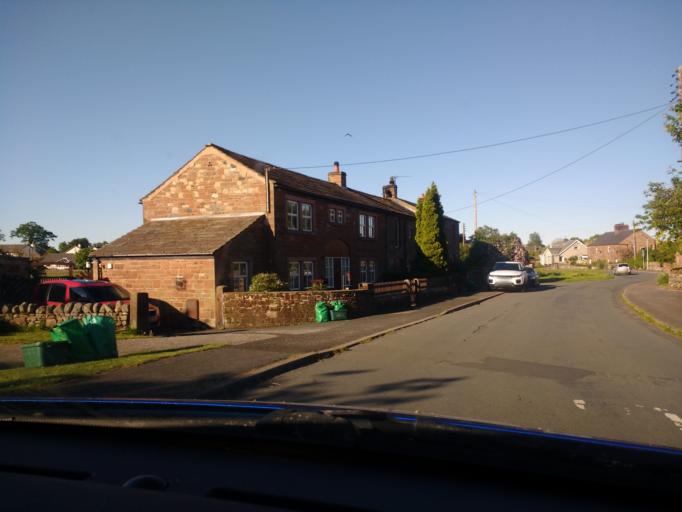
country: GB
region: England
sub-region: Cumbria
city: Appleby-in-Westmorland
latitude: 54.6606
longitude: -2.6030
